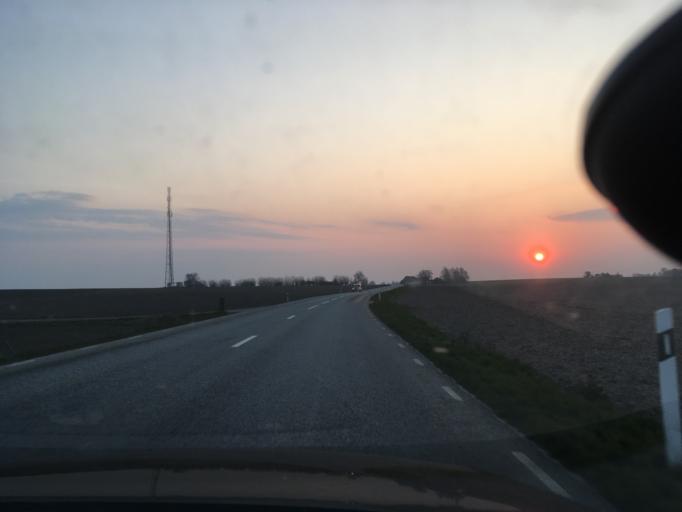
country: SE
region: Skane
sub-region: Ystads Kommun
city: Kopingebro
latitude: 55.4595
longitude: 14.0248
